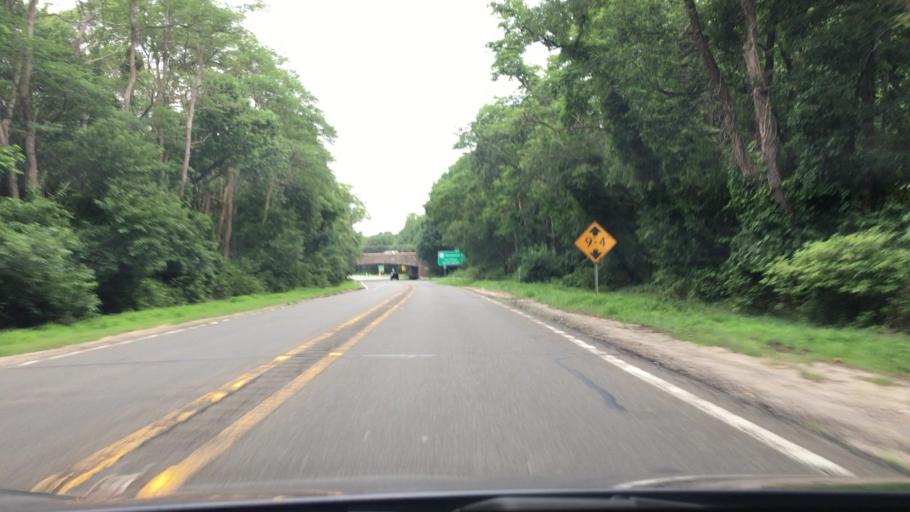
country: US
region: New York
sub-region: Nassau County
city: Plainedge
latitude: 40.7292
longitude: -73.4693
